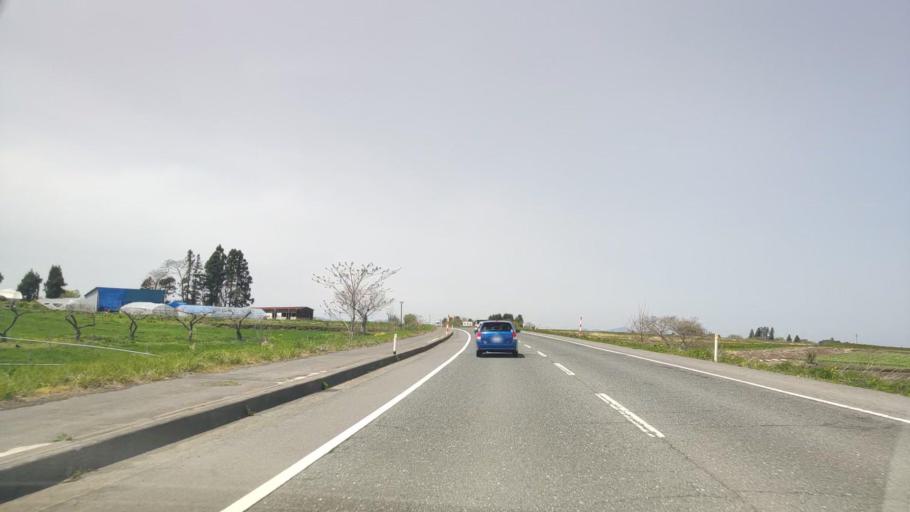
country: JP
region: Aomori
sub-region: Misawa Shi
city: Inuotose
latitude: 40.6364
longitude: 141.2424
